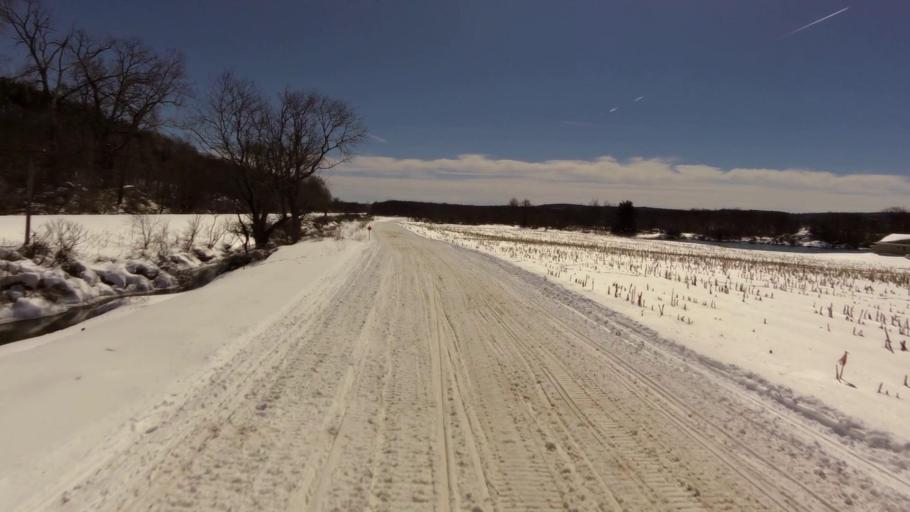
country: US
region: New York
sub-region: Cattaraugus County
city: Franklinville
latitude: 42.4008
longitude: -78.4737
